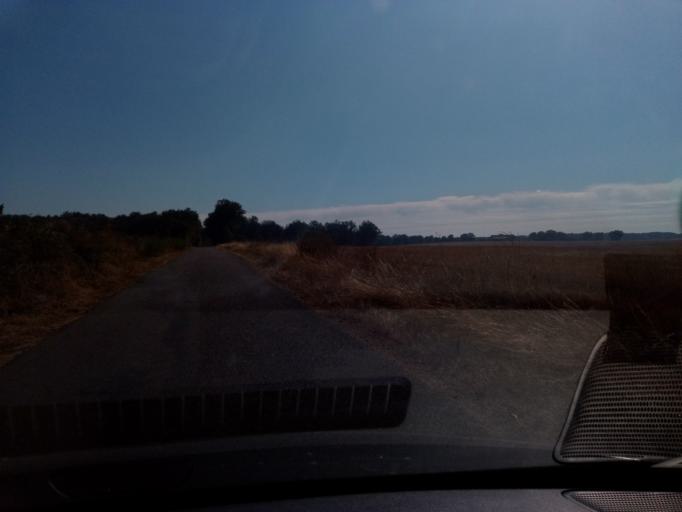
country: FR
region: Poitou-Charentes
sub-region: Departement de la Vienne
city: Lussac-les-Chateaux
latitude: 46.3817
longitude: 0.7880
